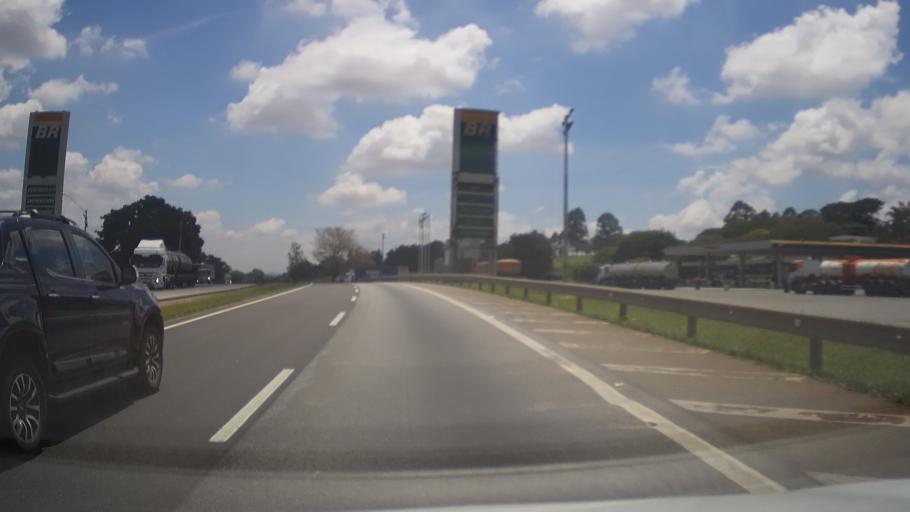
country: BR
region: Minas Gerais
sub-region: Sao Goncalo Do Sapucai
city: Sao Goncalo do Sapucai
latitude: -21.9461
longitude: -45.6205
